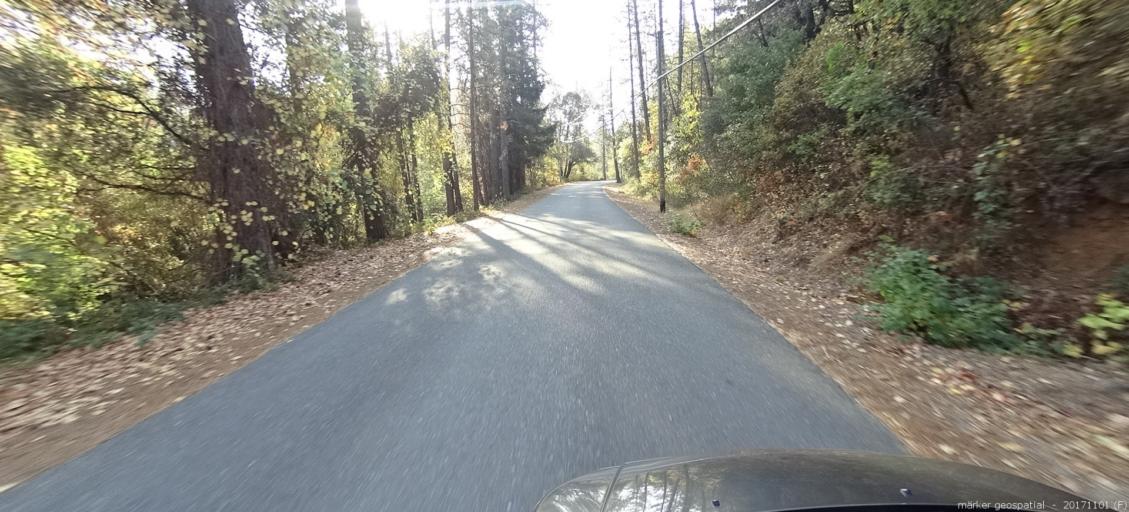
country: US
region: California
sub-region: Shasta County
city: Shasta Lake
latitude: 40.8126
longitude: -122.3259
